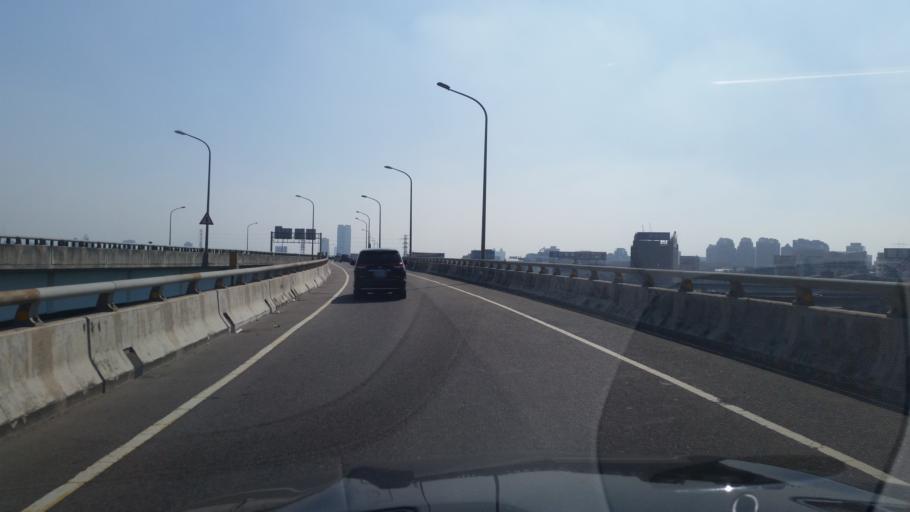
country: TW
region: Taipei
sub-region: Taipei
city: Banqiao
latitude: 25.0758
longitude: 121.4515
